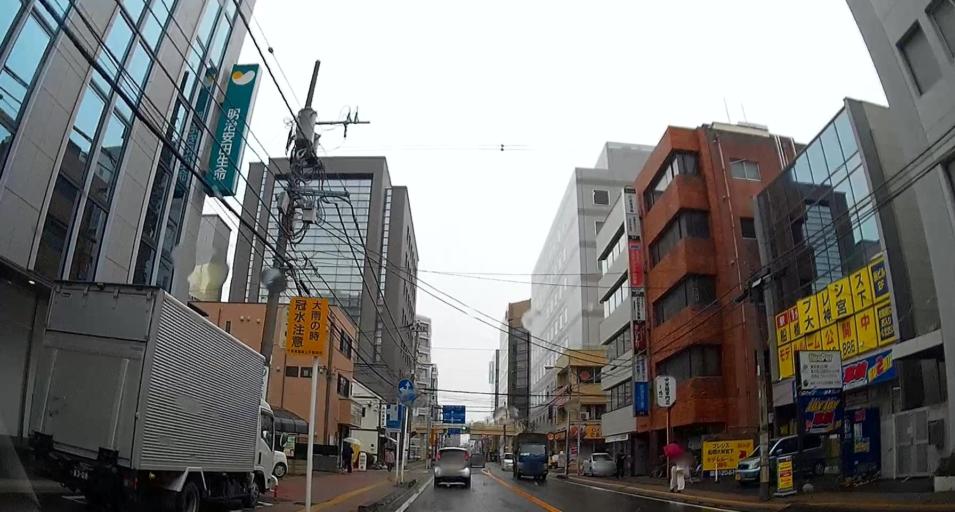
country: JP
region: Chiba
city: Funabashi
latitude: 35.6961
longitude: 139.9837
